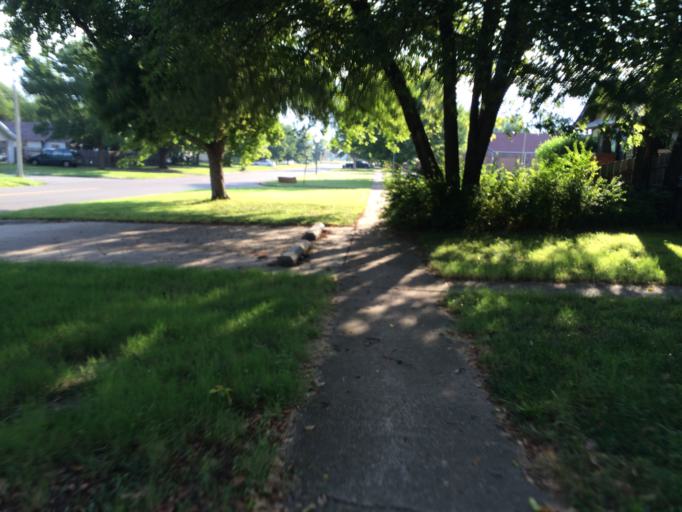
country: US
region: Oklahoma
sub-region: Cleveland County
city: Norman
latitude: 35.2241
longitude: -97.4354
